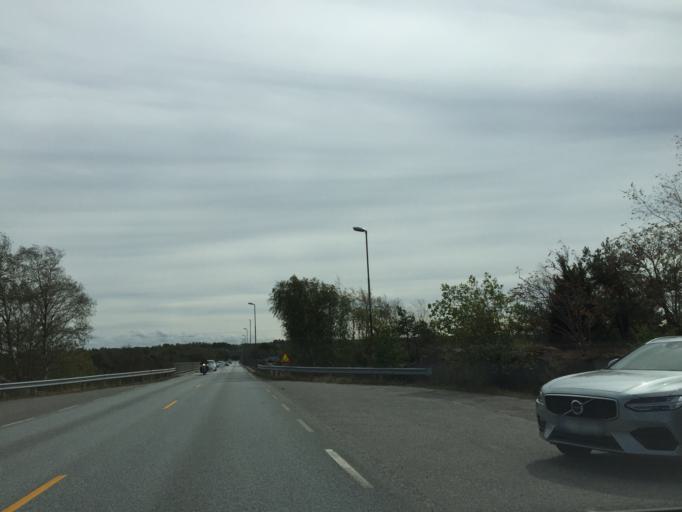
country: NO
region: Ostfold
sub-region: Hvaler
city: Skjaerhalden
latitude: 59.0794
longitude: 10.9318
